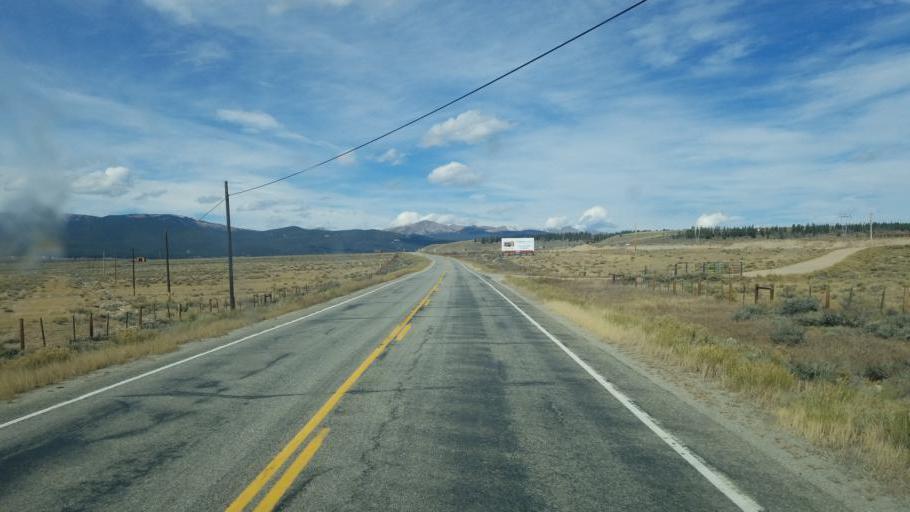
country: US
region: Colorado
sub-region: Lake County
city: Leadville
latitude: 39.1843
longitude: -106.3287
